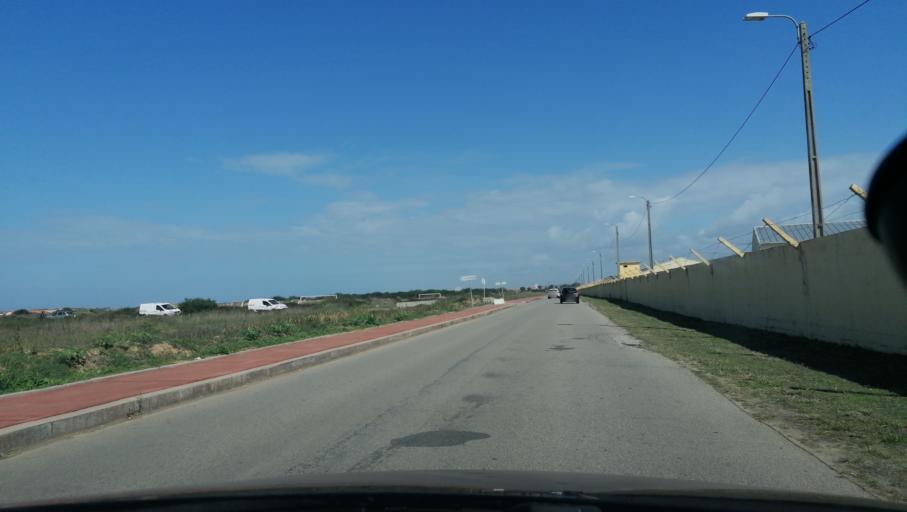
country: PT
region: Aveiro
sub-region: Espinho
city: Souto
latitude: 40.9761
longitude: -8.6437
